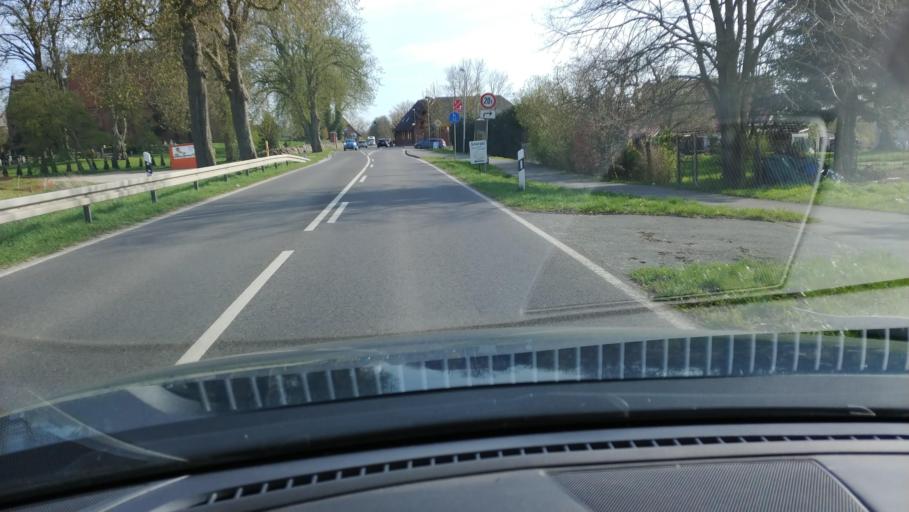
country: DE
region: Mecklenburg-Vorpommern
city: Seehof
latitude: 53.6919
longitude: 11.3959
